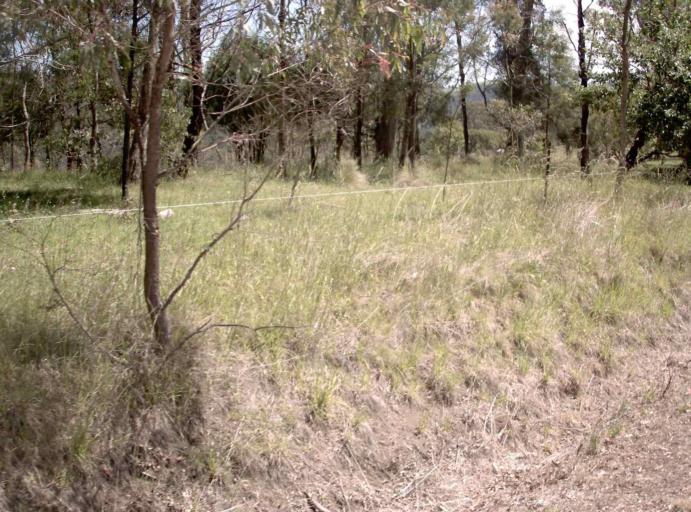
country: AU
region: Victoria
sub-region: East Gippsland
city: Lakes Entrance
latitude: -37.3361
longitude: 148.2312
